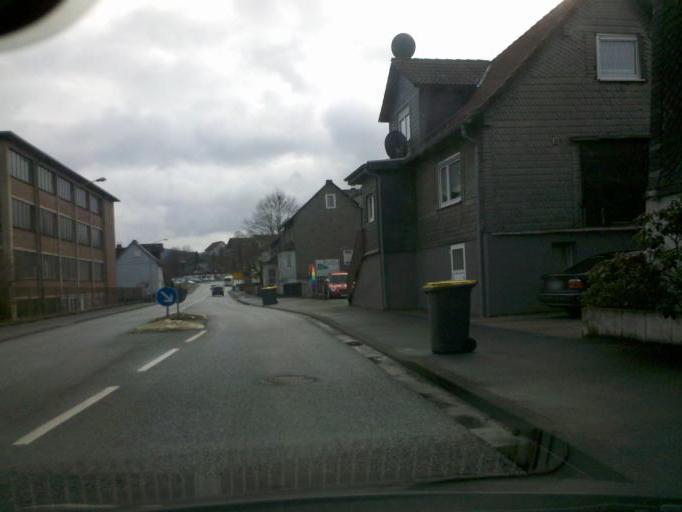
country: DE
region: Hesse
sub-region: Regierungsbezirk Giessen
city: Biedenkopf
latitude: 50.8655
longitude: 8.5507
